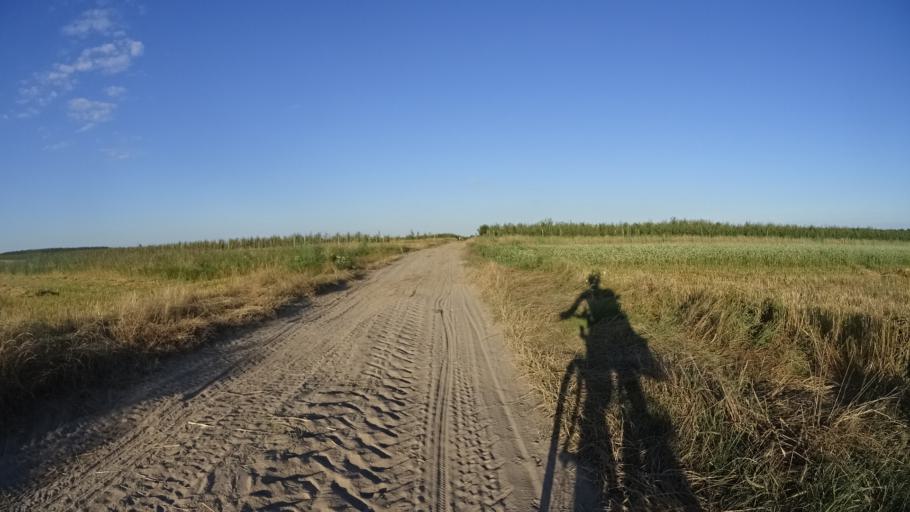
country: PL
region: Masovian Voivodeship
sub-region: Powiat bialobrzeski
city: Wysmierzyce
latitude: 51.6588
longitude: 20.7932
